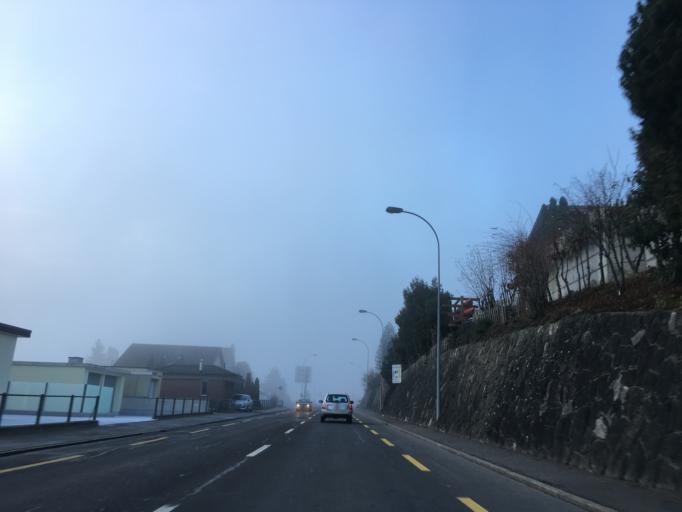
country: CH
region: Schwyz
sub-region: Bezirk Kuessnacht
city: Kussnacht
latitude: 47.0803
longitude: 8.4317
